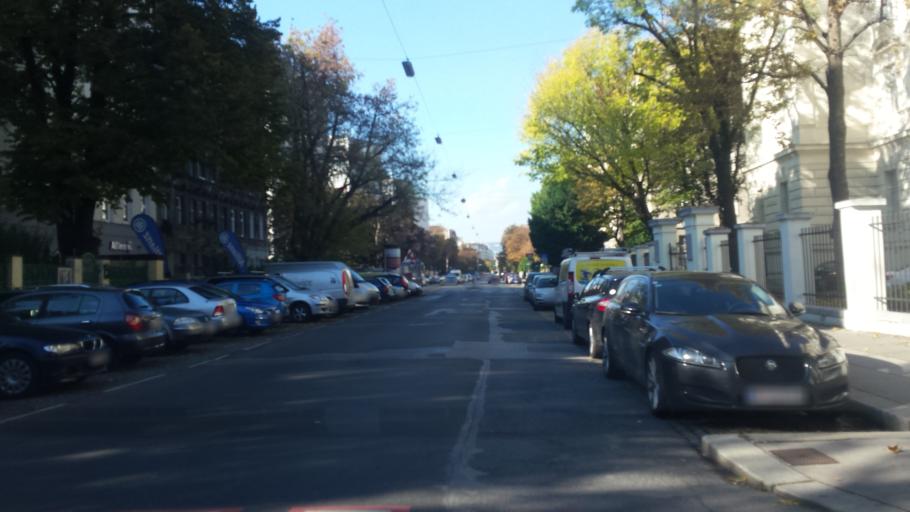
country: AT
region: Vienna
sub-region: Wien Stadt
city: Vienna
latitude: 48.2205
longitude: 16.4067
